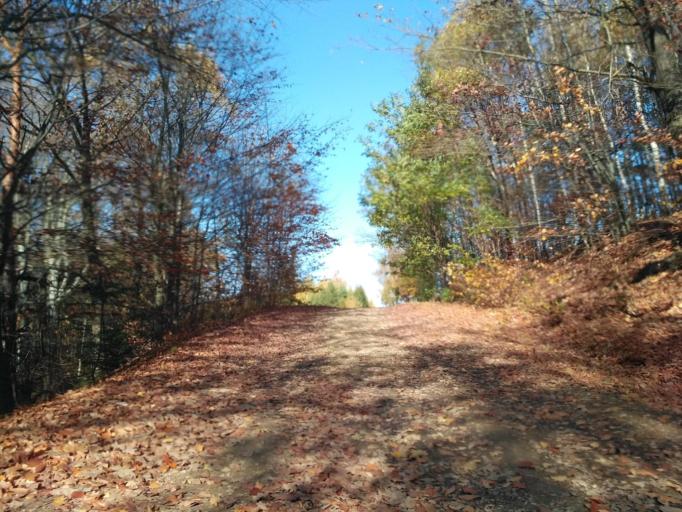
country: PL
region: Subcarpathian Voivodeship
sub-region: Powiat rzeszowski
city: Blazowa
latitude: 49.8628
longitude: 22.0855
